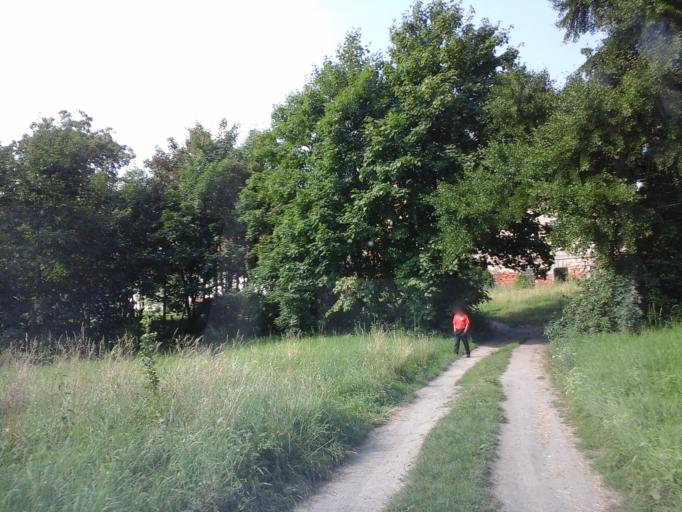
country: PL
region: West Pomeranian Voivodeship
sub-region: Powiat choszczenski
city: Pelczyce
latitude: 53.0654
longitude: 15.2447
